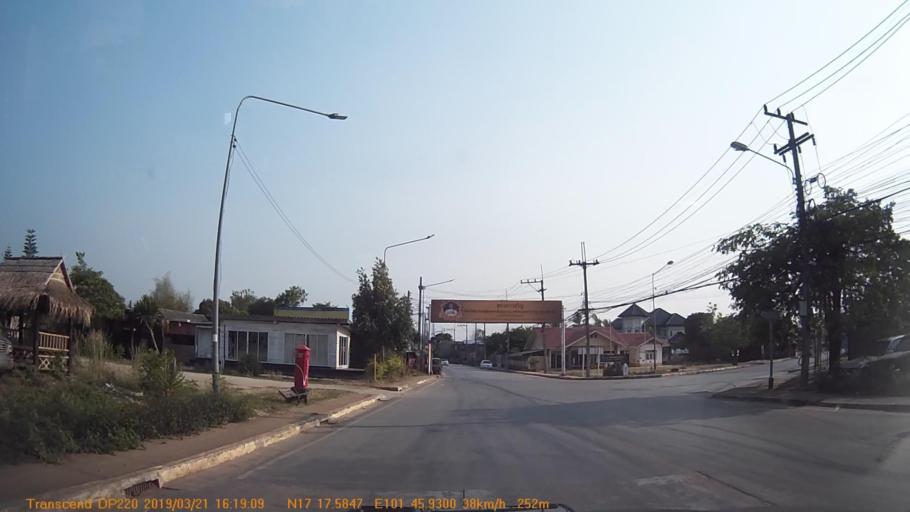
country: TH
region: Loei
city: Wang Saphung
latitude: 17.2929
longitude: 101.7655
